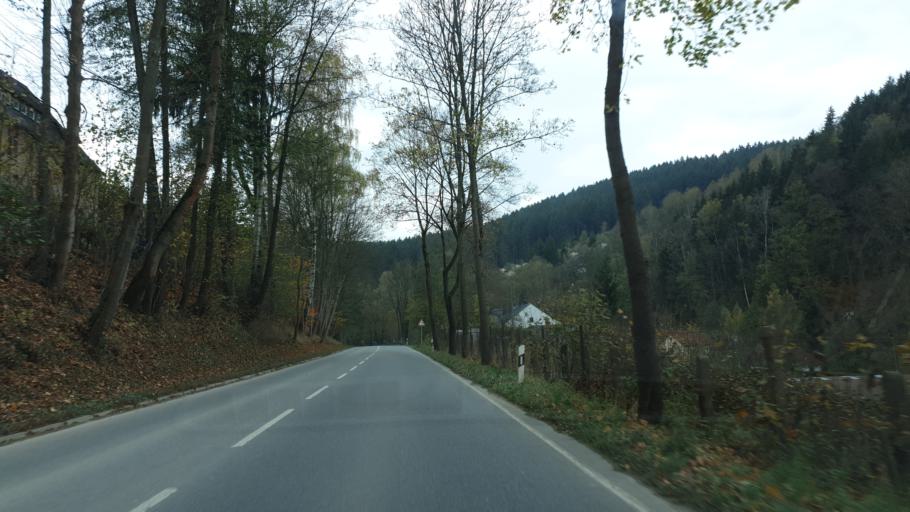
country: DE
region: Saxony
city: Schwarzenberg
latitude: 50.5162
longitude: 12.7786
